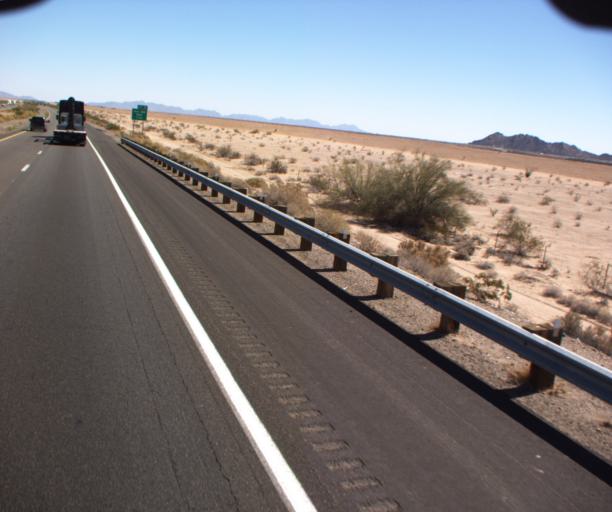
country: US
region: Arizona
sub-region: Yuma County
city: Wellton
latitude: 32.6768
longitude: -114.0446
